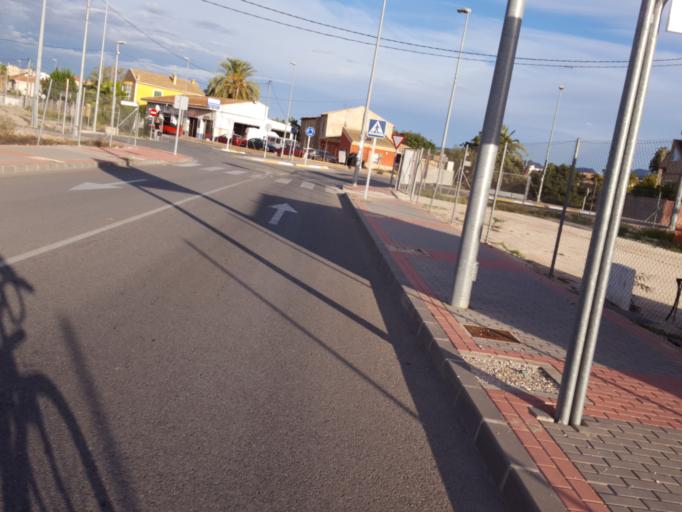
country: ES
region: Murcia
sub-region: Murcia
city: Murcia
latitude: 37.9883
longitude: -1.1506
